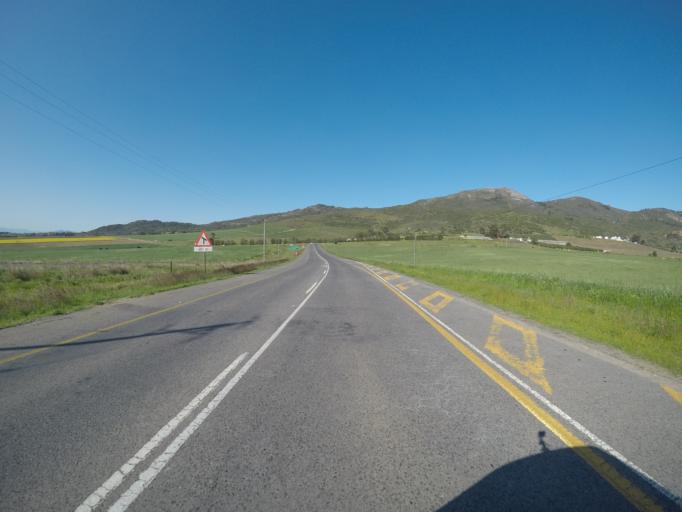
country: ZA
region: Western Cape
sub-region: Cape Winelands District Municipality
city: Noorder-Paarl
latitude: -33.7081
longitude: 18.8892
